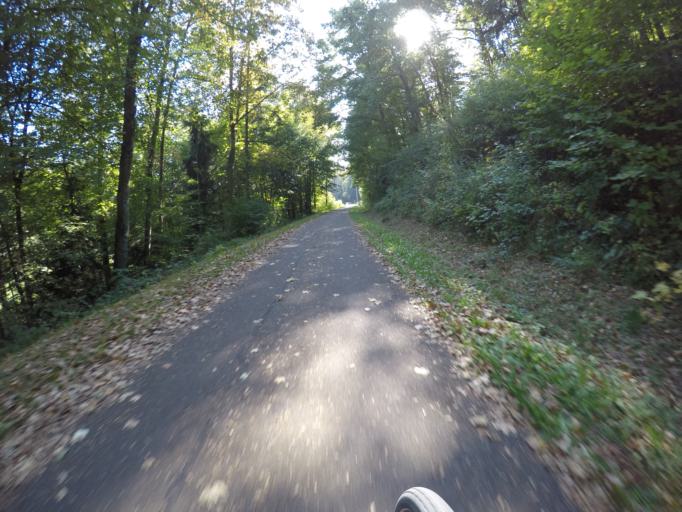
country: DE
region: Baden-Wuerttemberg
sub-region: Regierungsbezirk Stuttgart
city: Steinenbronn
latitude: 48.6832
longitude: 9.1271
